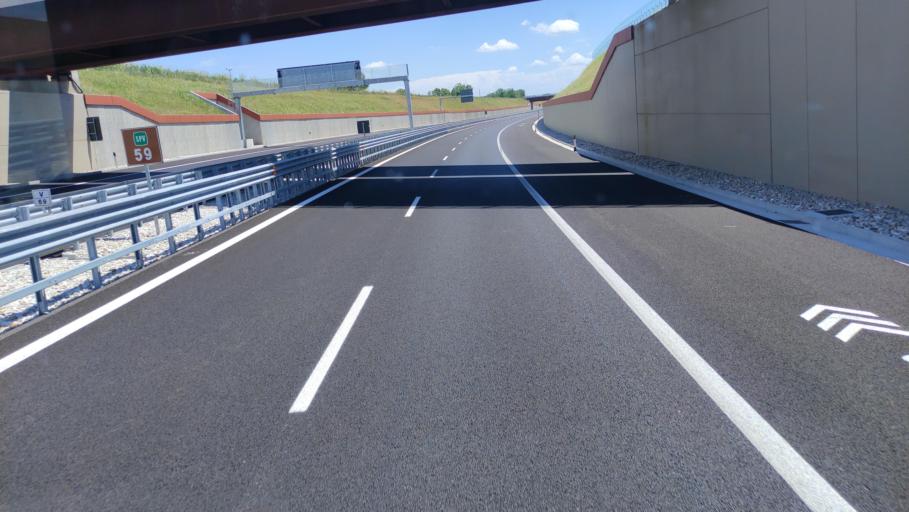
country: IT
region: Veneto
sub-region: Provincia di Treviso
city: Caselle
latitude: 45.7300
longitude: 11.9783
